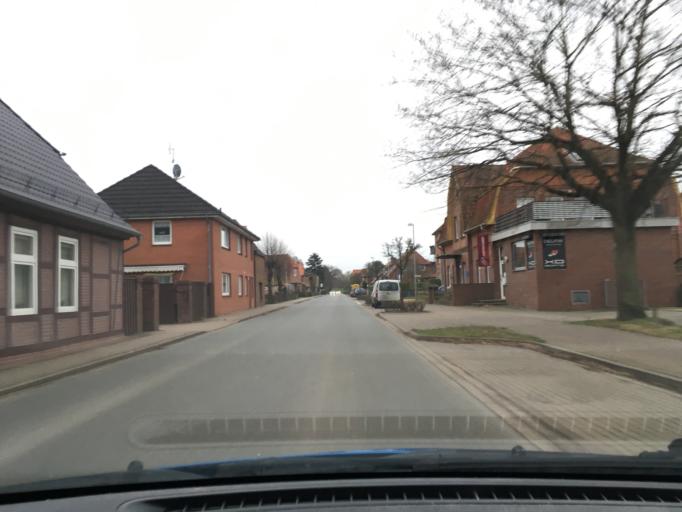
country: DE
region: Lower Saxony
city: Bleckede
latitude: 53.2904
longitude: 10.7345
